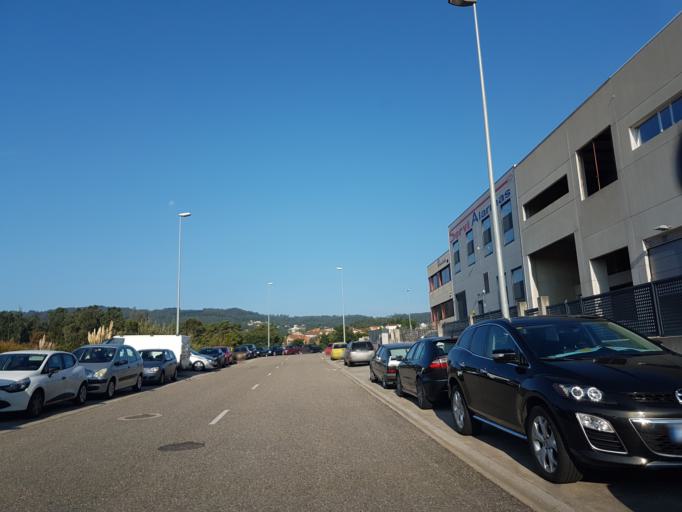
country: ES
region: Galicia
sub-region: Provincia de Pontevedra
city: Porrino
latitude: 42.1890
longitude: -8.6245
